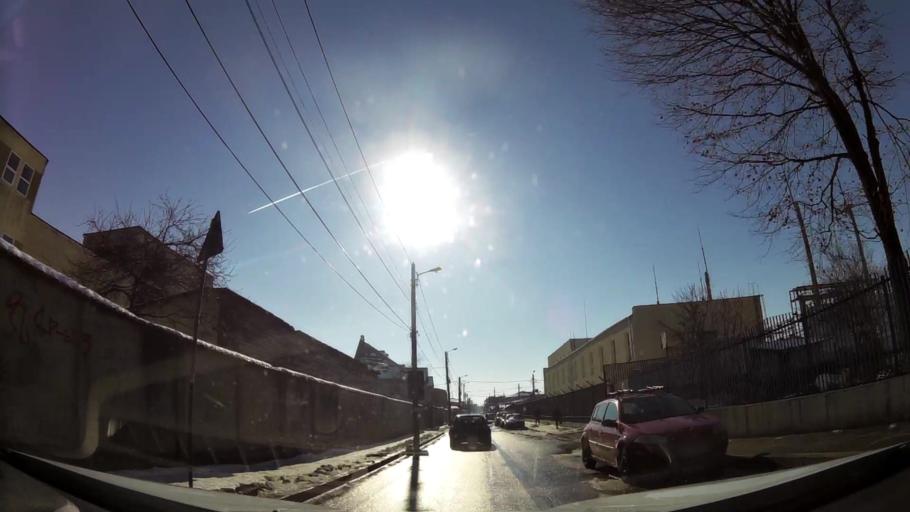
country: RO
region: Bucuresti
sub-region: Municipiul Bucuresti
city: Bucuresti
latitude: 44.4019
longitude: 26.0597
